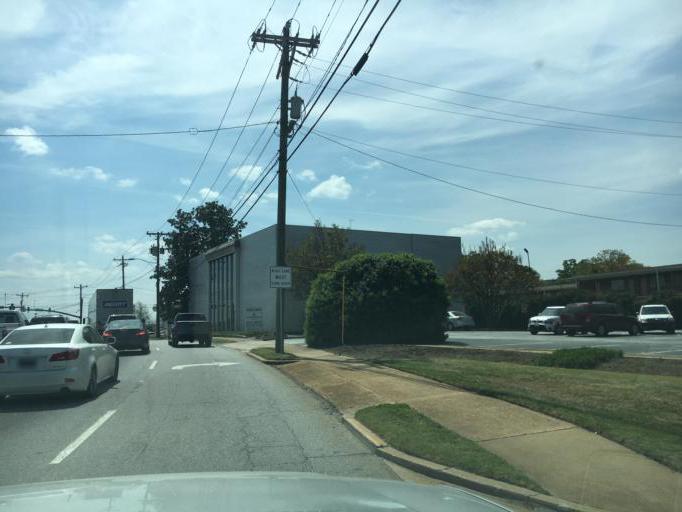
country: US
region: South Carolina
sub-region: Spartanburg County
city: Spartanburg
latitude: 34.9532
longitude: -81.9210
